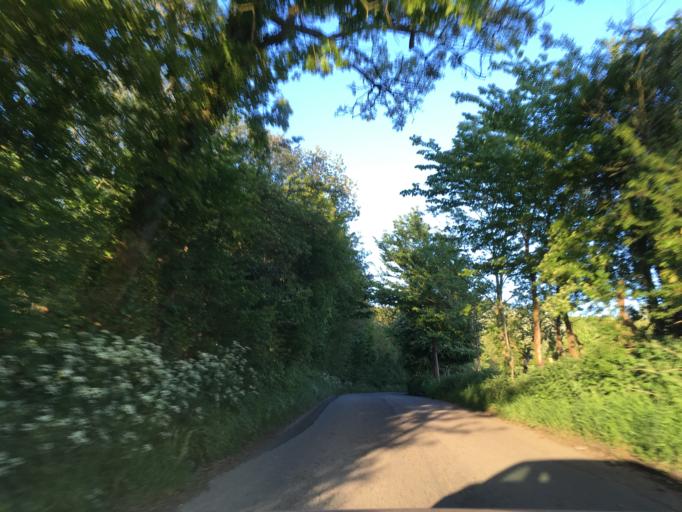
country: GB
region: Wales
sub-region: Newport
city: Llanwern
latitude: 51.5863
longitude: -2.9084
